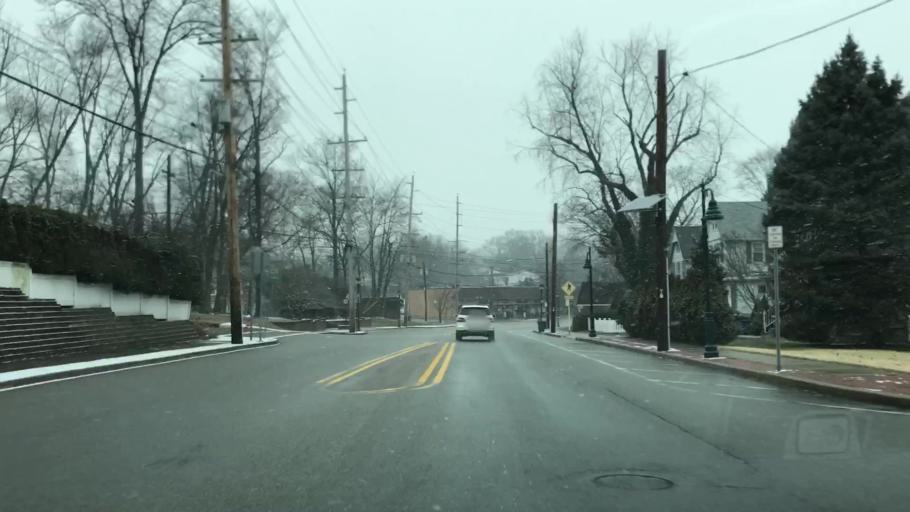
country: US
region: New Jersey
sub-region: Bergen County
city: Oradell
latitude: 40.9473
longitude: -74.0300
